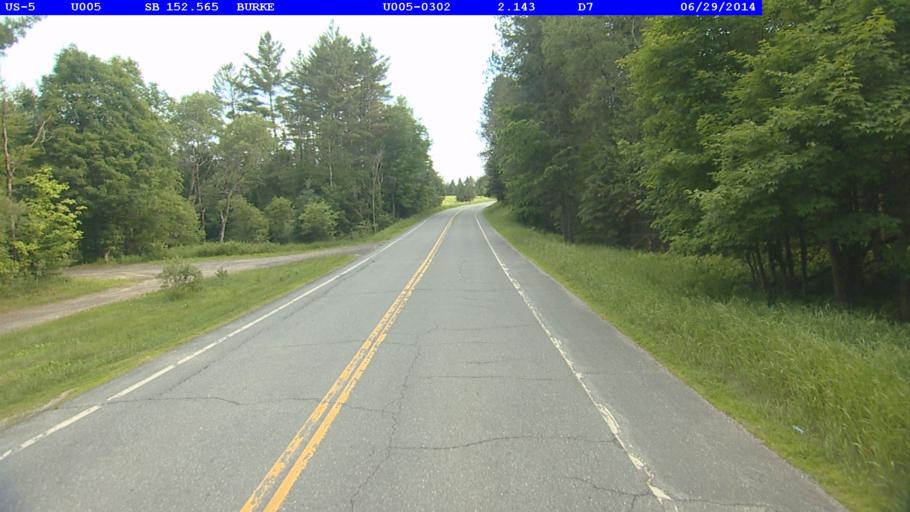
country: US
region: Vermont
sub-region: Caledonia County
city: Lyndonville
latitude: 44.6157
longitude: -71.9723
